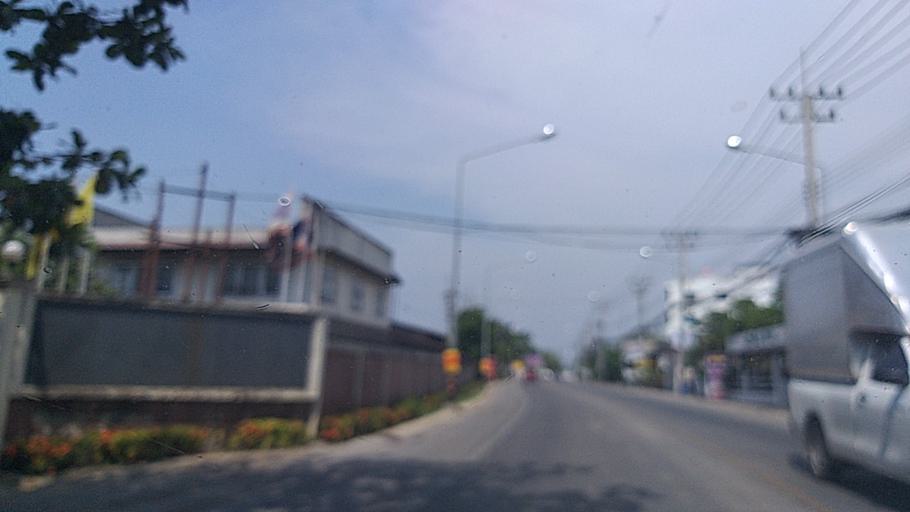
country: TH
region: Nakhon Pathom
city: Sam Phran
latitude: 13.7424
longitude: 100.2693
